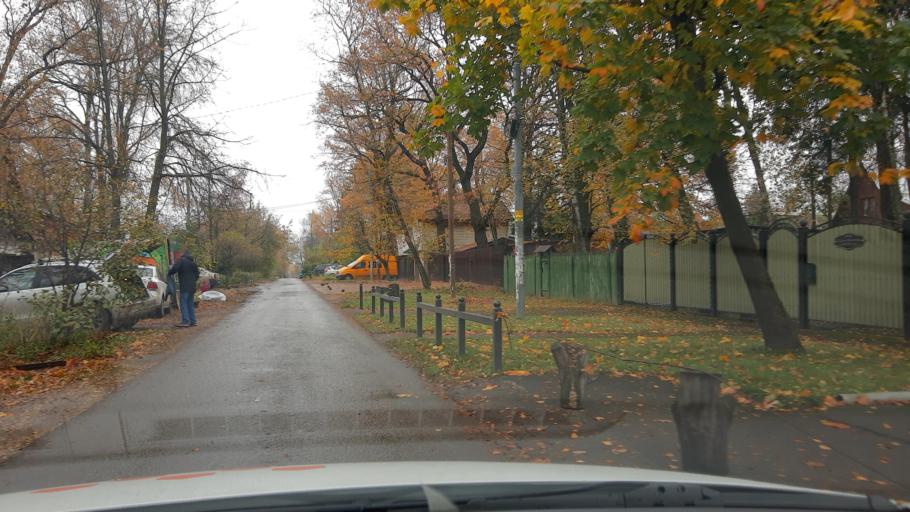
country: RU
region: Moscow
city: Mikhalkovo
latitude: 55.6707
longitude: 37.4185
